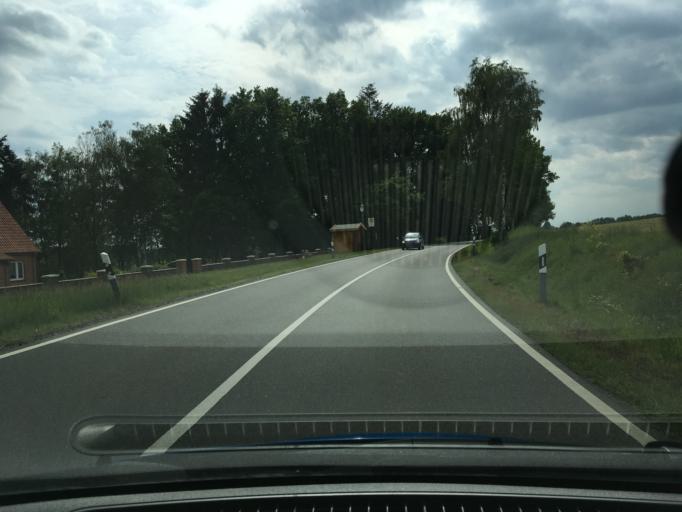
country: DE
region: Lower Saxony
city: Betzendorf
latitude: 53.1056
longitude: 10.2988
